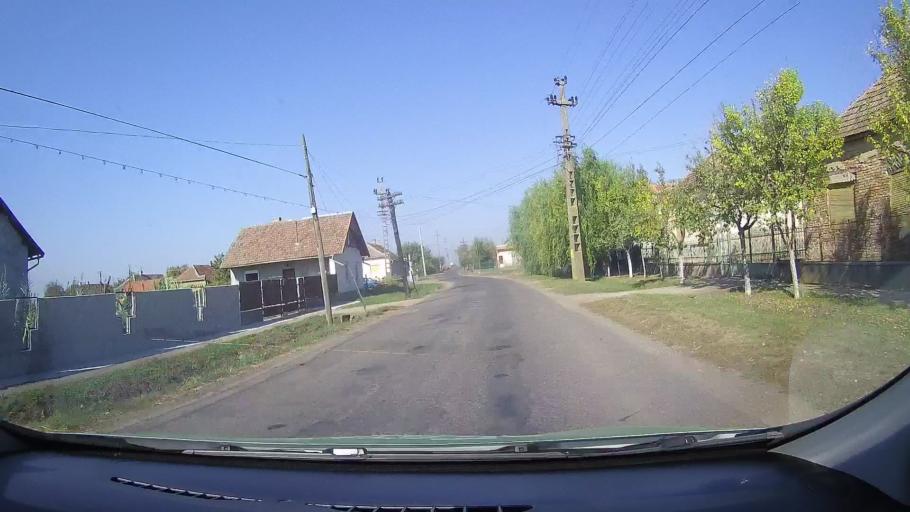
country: RO
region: Satu Mare
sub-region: Comuna Petresti
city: Petresti
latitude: 47.6082
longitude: 22.3580
